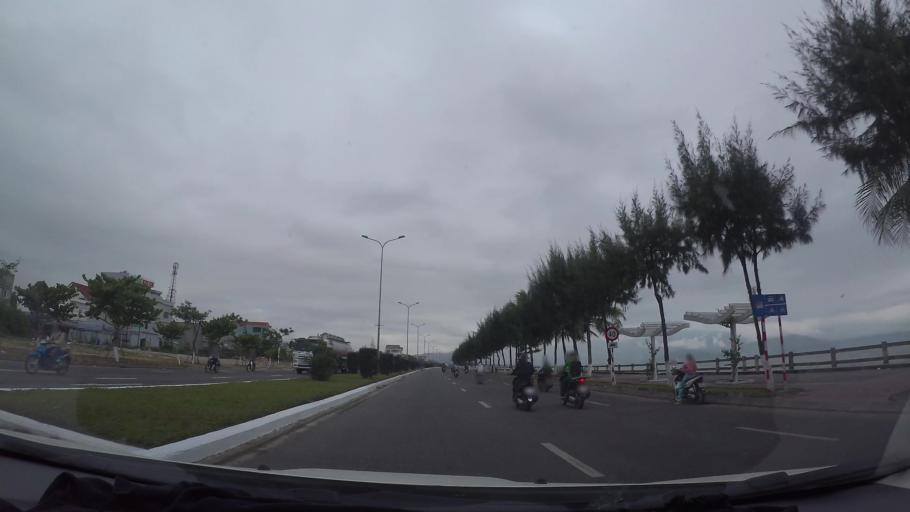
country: VN
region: Da Nang
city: Lien Chieu
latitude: 16.0843
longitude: 108.1612
